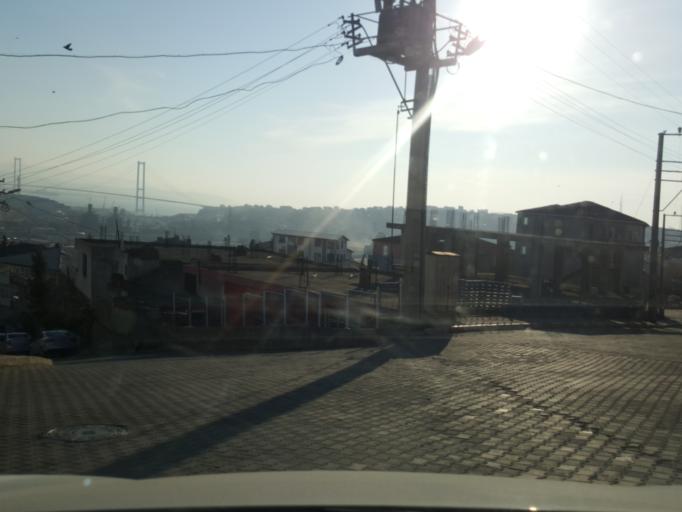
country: TR
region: Kocaeli
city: Tavsancil
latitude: 40.7872
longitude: 29.5424
